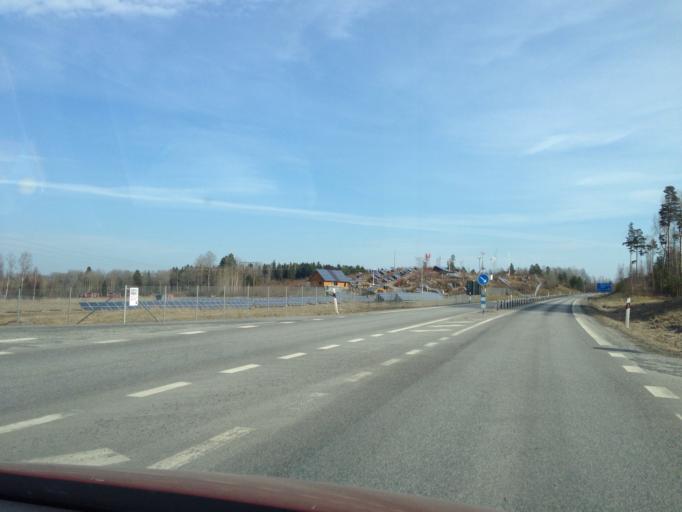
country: SE
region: Soedermanland
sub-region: Katrineholms Kommun
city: Katrineholm
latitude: 59.0074
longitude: 16.2023
